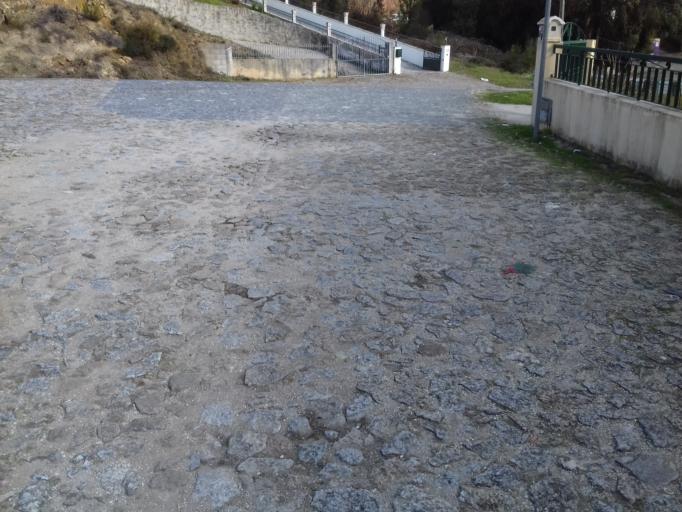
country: PT
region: Braga
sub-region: Cabeceiras de Basto
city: Refojos de Basto
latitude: 41.5288
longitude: -8.0112
